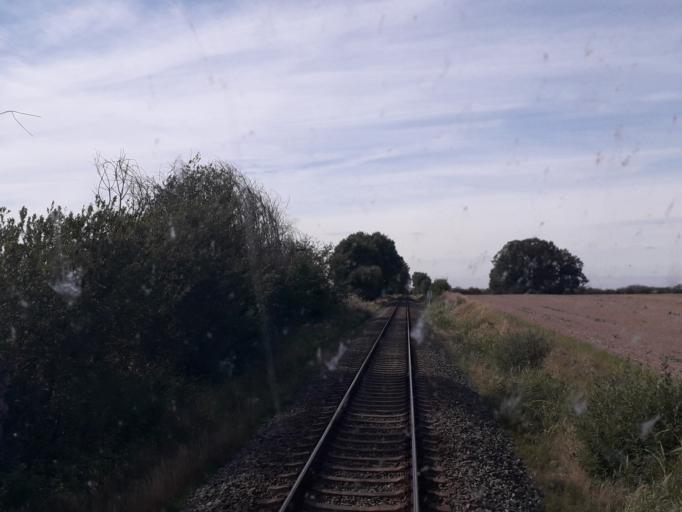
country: DE
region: Brandenburg
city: Neuruppin
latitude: 52.8698
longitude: 12.8683
